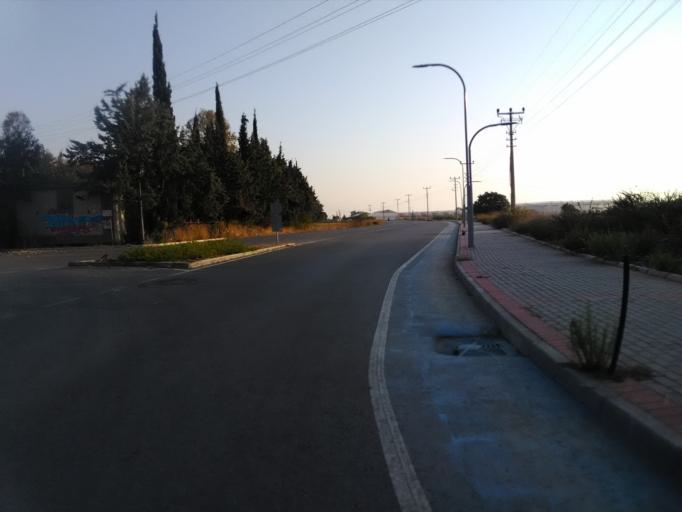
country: TR
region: Antalya
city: Gazipasa
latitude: 36.2593
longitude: 32.2904
